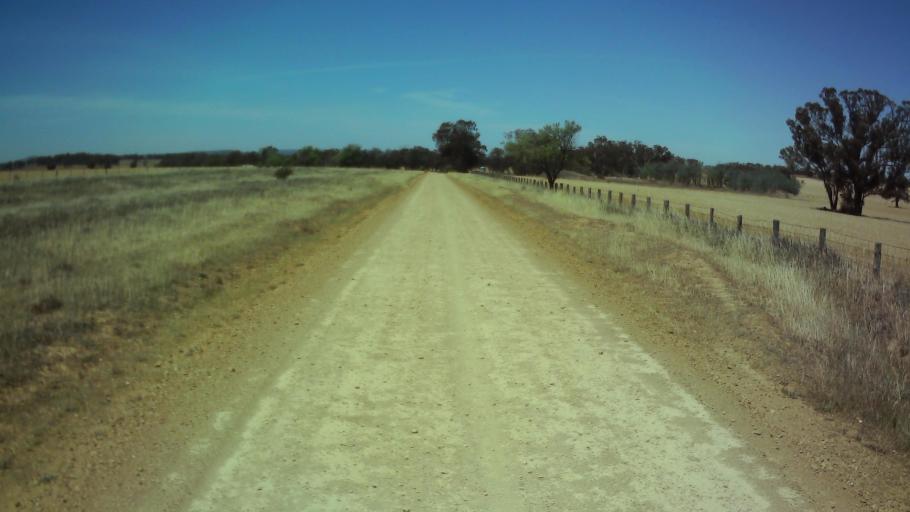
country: AU
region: New South Wales
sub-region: Weddin
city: Grenfell
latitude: -33.9239
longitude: 148.1845
